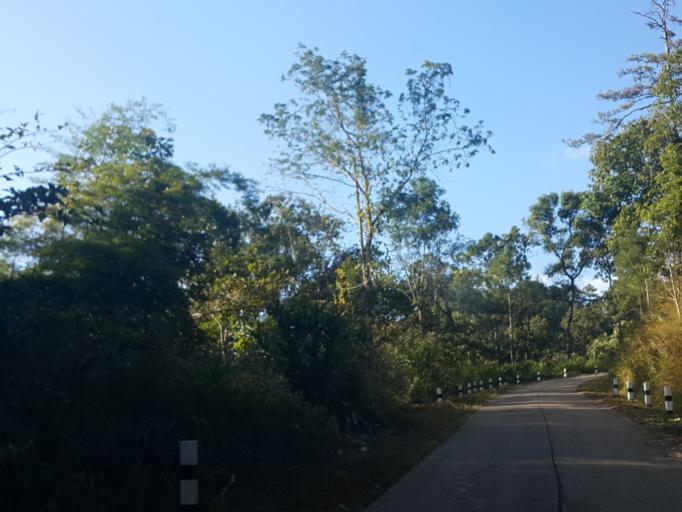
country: TH
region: Chiang Mai
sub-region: Amphoe Chiang Dao
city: Chiang Dao
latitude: 19.4129
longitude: 98.8603
